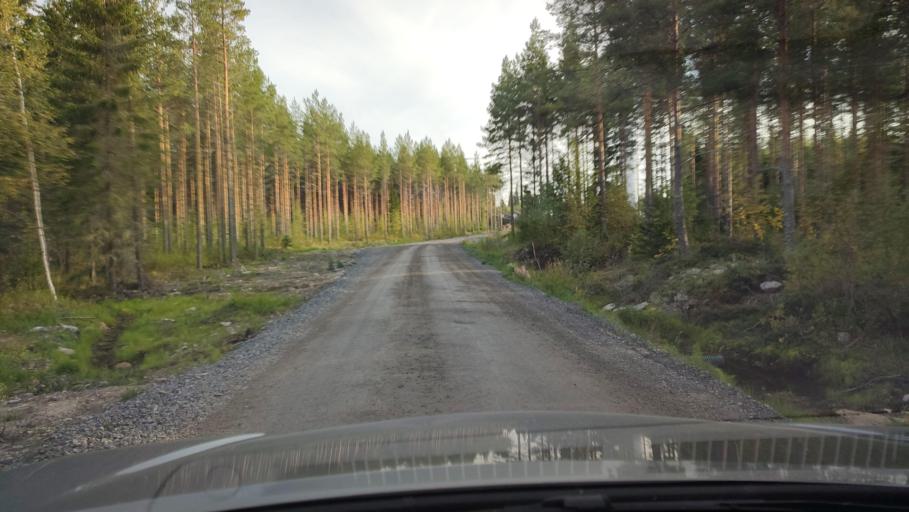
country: FI
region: Southern Ostrobothnia
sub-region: Suupohja
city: Karijoki
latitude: 62.1781
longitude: 21.5909
